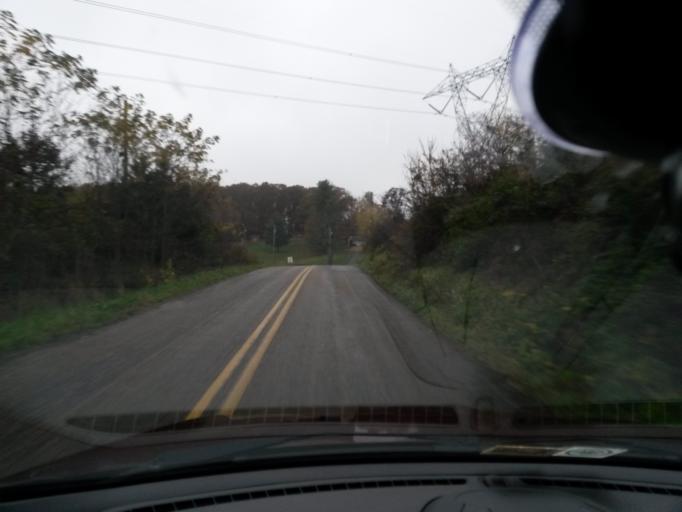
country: US
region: Virginia
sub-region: Botetourt County
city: Fincastle
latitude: 37.4723
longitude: -79.8445
